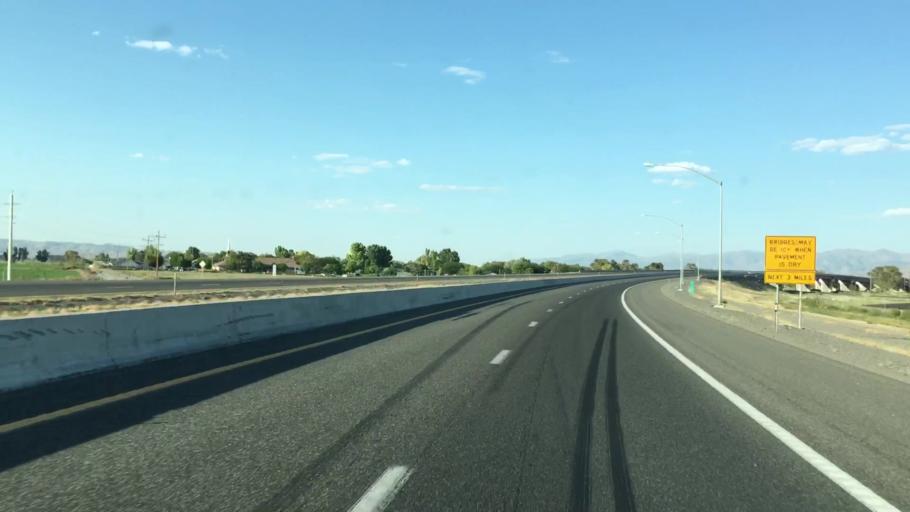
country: US
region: Nevada
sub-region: Pershing County
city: Lovelock
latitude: 40.1659
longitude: -118.4858
